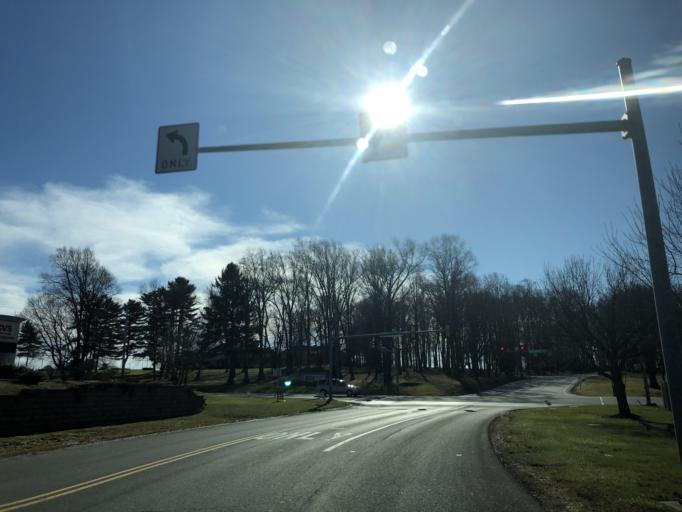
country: US
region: Pennsylvania
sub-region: Chester County
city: Oxford
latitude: 39.7503
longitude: -76.0217
